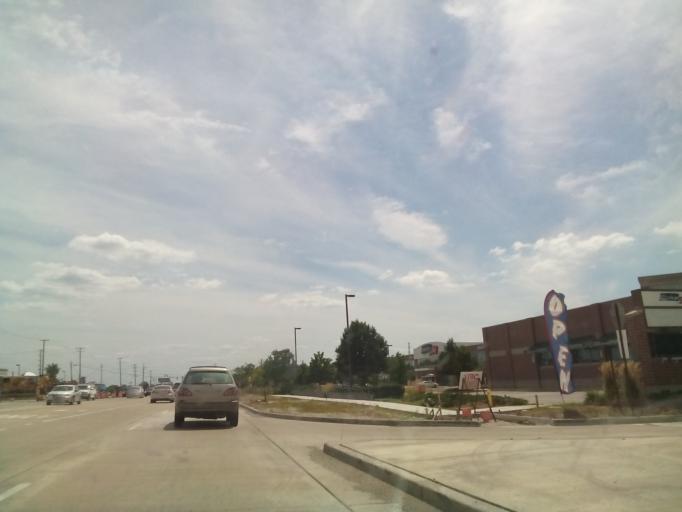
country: US
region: Illinois
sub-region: DuPage County
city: Warrenville
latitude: 41.7837
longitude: -88.2059
